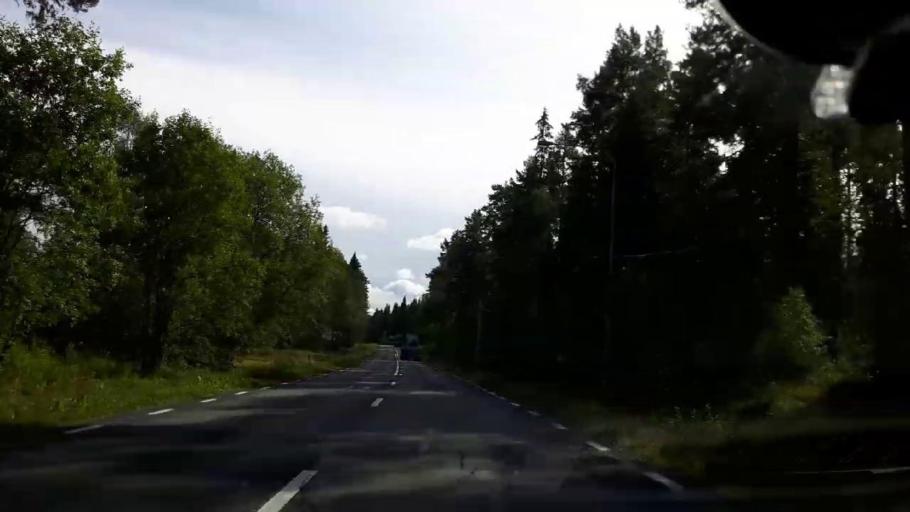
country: SE
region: Jaemtland
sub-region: Braecke Kommun
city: Braecke
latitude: 63.1710
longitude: 15.5446
